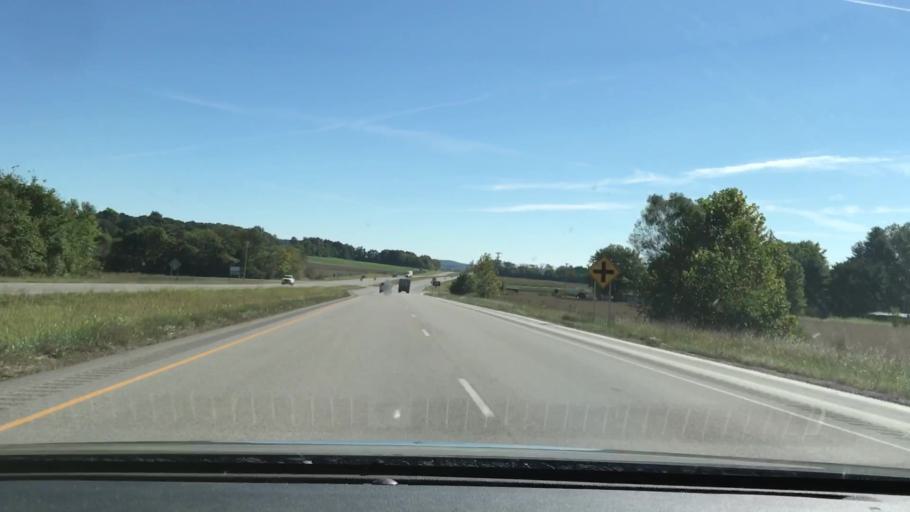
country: US
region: Kentucky
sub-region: Todd County
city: Elkton
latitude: 36.8471
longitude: -87.3041
